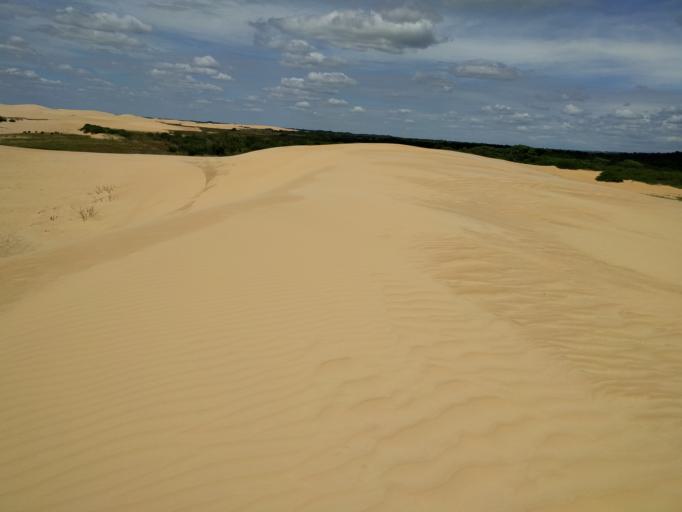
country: BO
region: Santa Cruz
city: Santa Cruz de la Sierra
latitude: -17.9501
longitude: -63.1580
